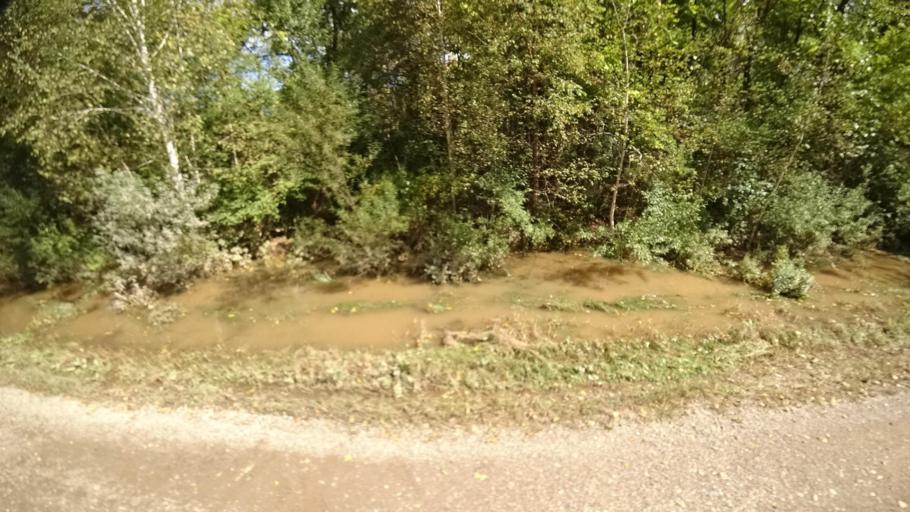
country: RU
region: Primorskiy
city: Yakovlevka
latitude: 44.6648
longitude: 133.7507
